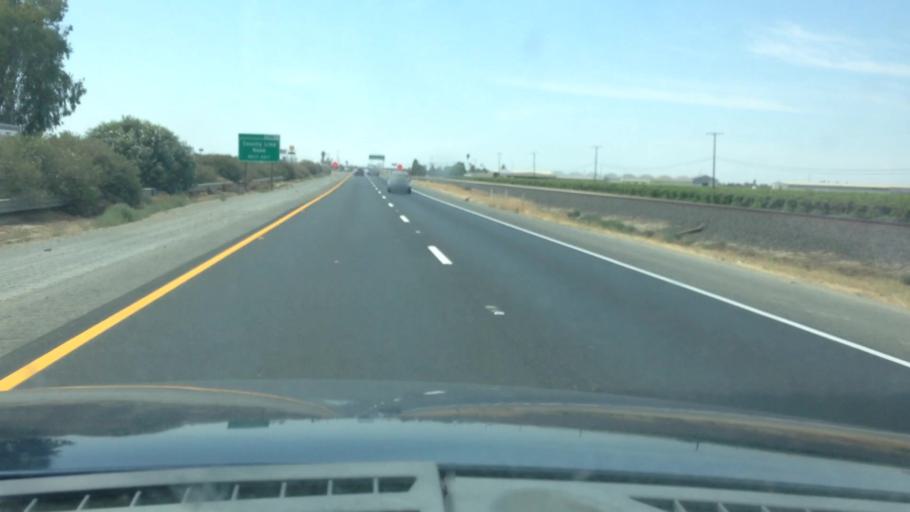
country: US
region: California
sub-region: Kern County
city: Delano
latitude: 35.7983
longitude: -119.2545
